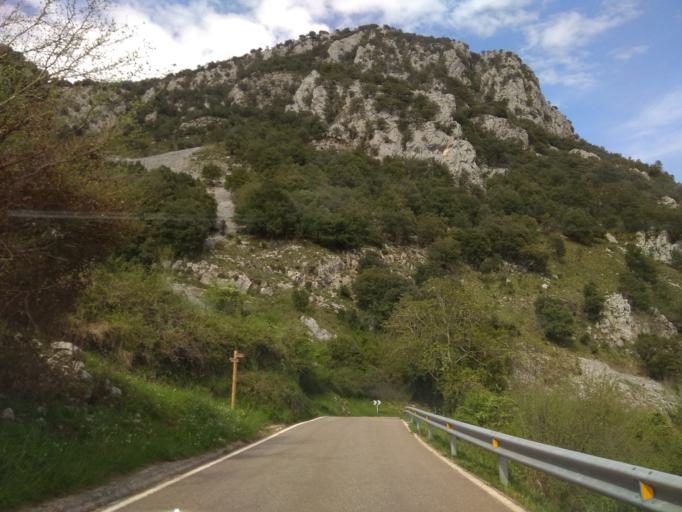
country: ES
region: Cantabria
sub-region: Provincia de Cantabria
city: Tresviso
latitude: 43.2553
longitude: -4.5758
